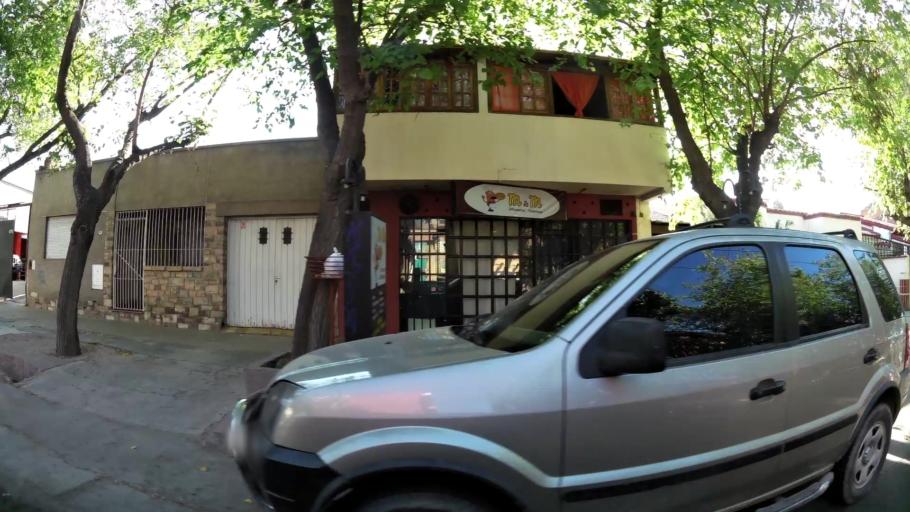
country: AR
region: Mendoza
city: Mendoza
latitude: -32.9031
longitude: -68.8288
